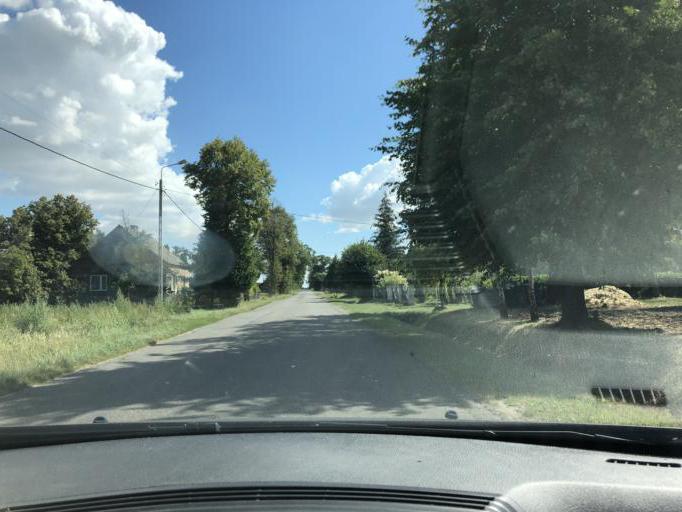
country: PL
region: Lodz Voivodeship
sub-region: Powiat wieruszowski
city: Czastary
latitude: 51.2607
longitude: 18.3598
